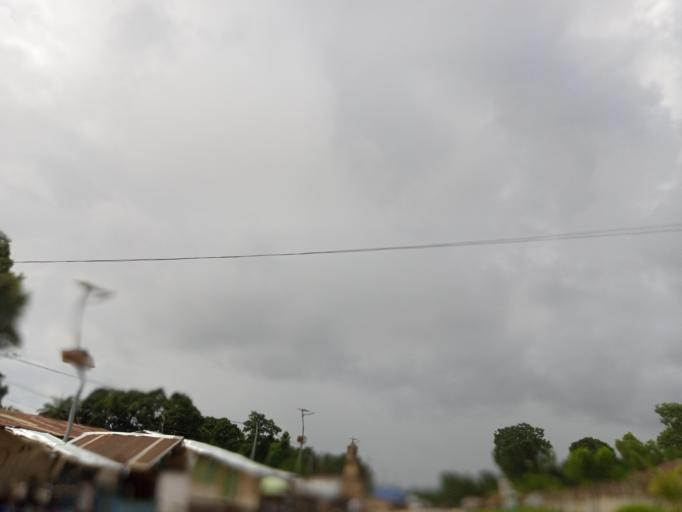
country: SL
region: Northern Province
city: Sawkta
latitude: 8.6275
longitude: -13.2053
